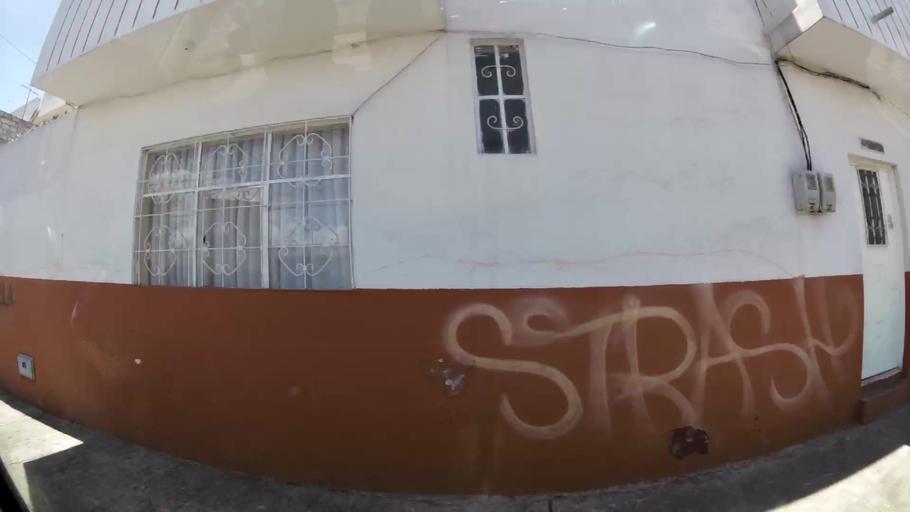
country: EC
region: Chimborazo
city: Riobamba
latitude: -1.6773
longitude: -78.6572
